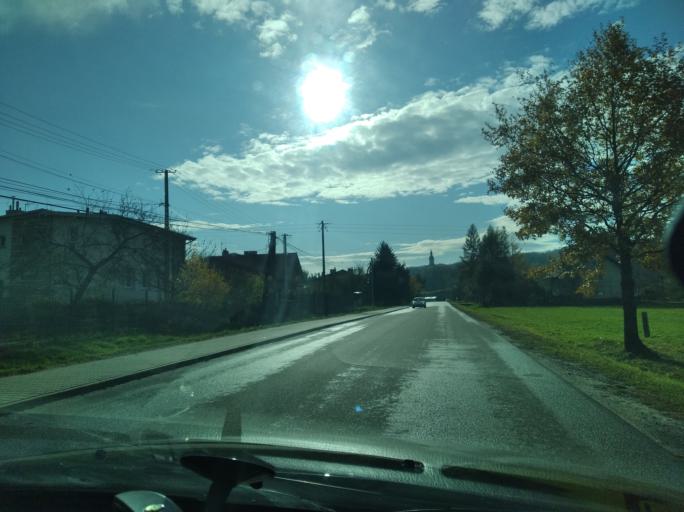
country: PL
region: Subcarpathian Voivodeship
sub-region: Powiat debicki
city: Brzeznica
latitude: 50.0549
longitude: 21.4842
